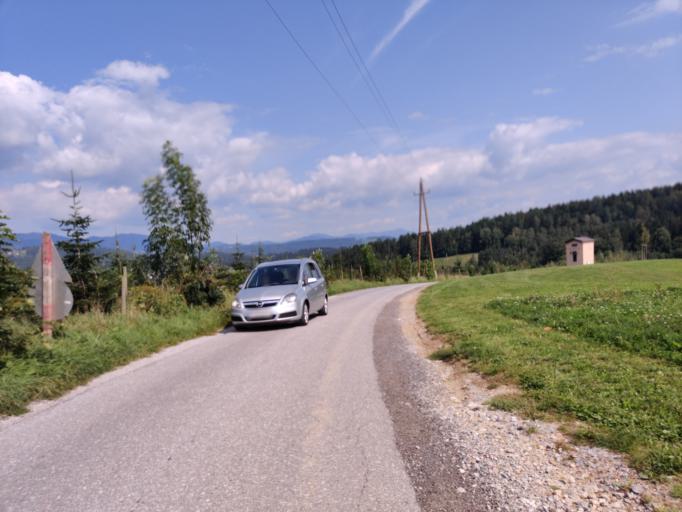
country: AT
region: Styria
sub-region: Graz Stadt
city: Mariatrost
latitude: 47.1277
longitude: 15.4986
